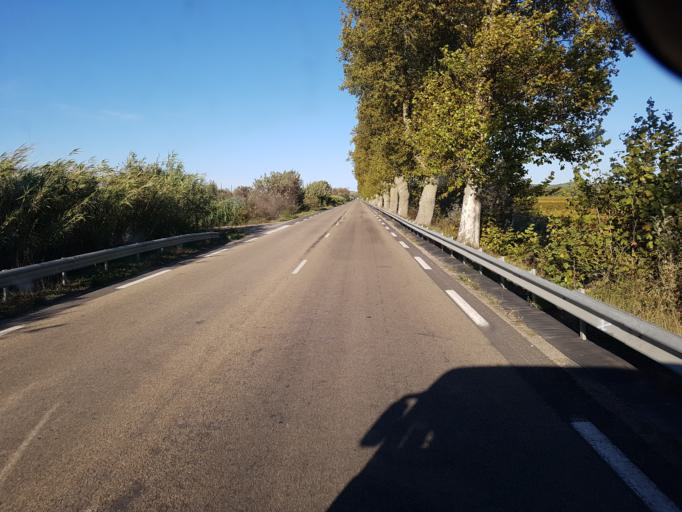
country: FR
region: Languedoc-Roussillon
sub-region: Departement de l'Aude
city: Coursan
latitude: 43.2451
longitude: 3.0645
